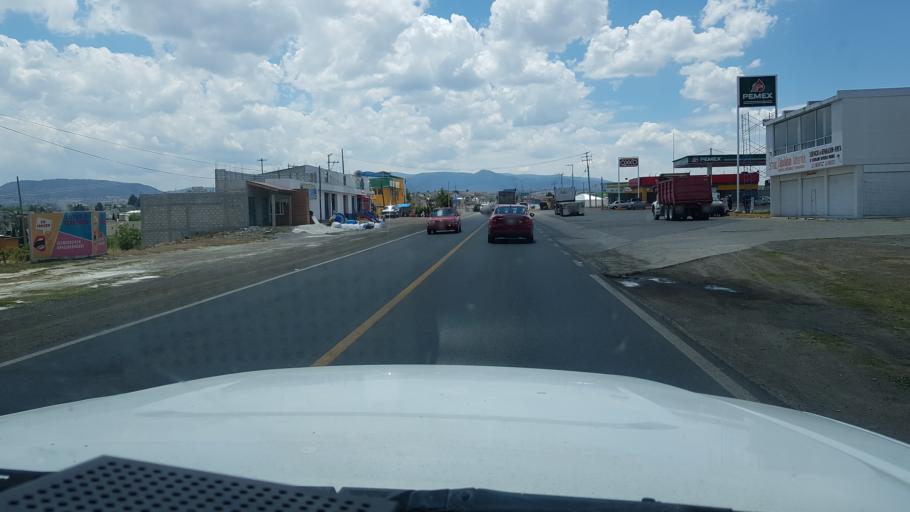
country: MX
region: Hidalgo
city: Calpulalpan
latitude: 19.5959
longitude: -98.5724
